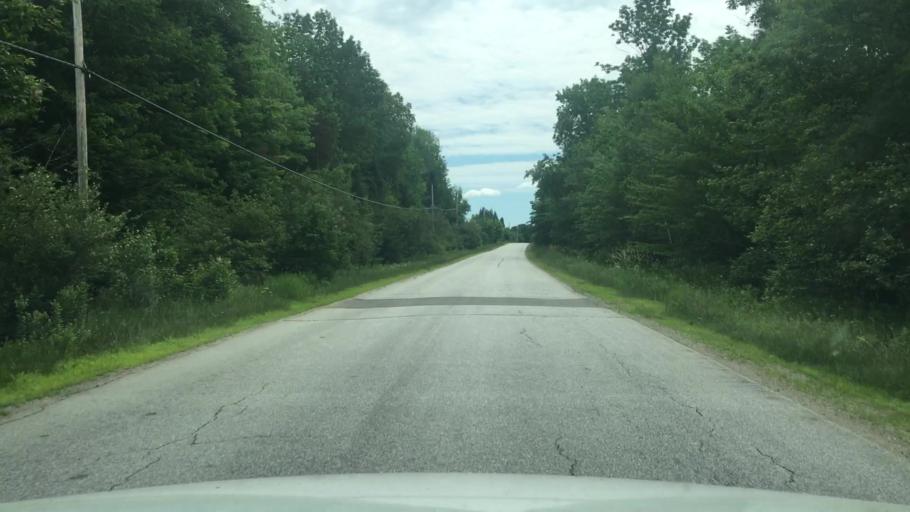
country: US
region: Maine
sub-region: Waldo County
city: Searsmont
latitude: 44.4551
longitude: -69.2582
